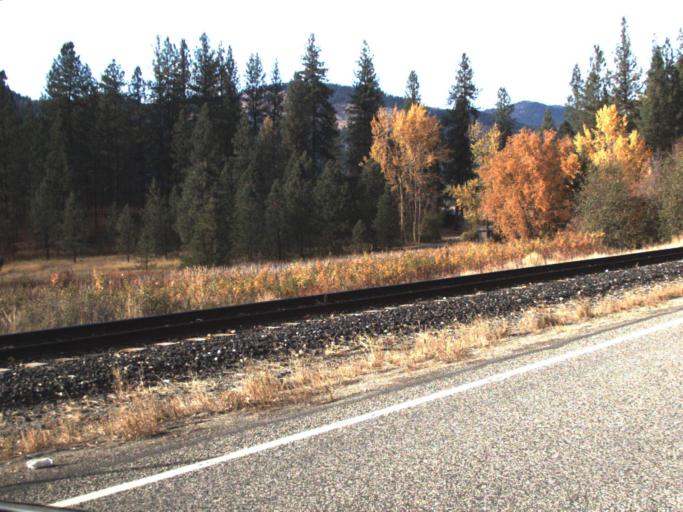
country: US
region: Washington
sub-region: Stevens County
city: Kettle Falls
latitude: 48.7848
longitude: -118.0010
